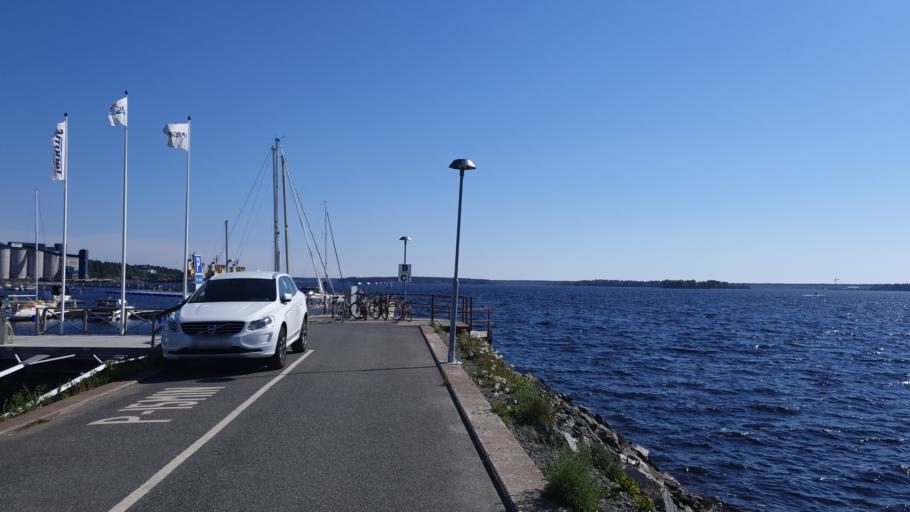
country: SE
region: Norrbotten
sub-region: Lulea Kommun
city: Lulea
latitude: 65.5798
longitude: 22.1602
